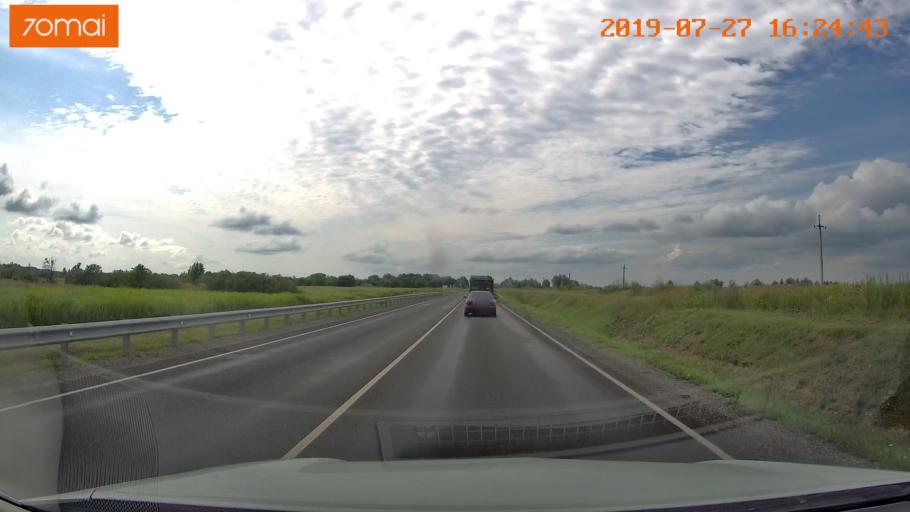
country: RU
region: Kaliningrad
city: Zheleznodorozhnyy
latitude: 54.6350
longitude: 21.4465
